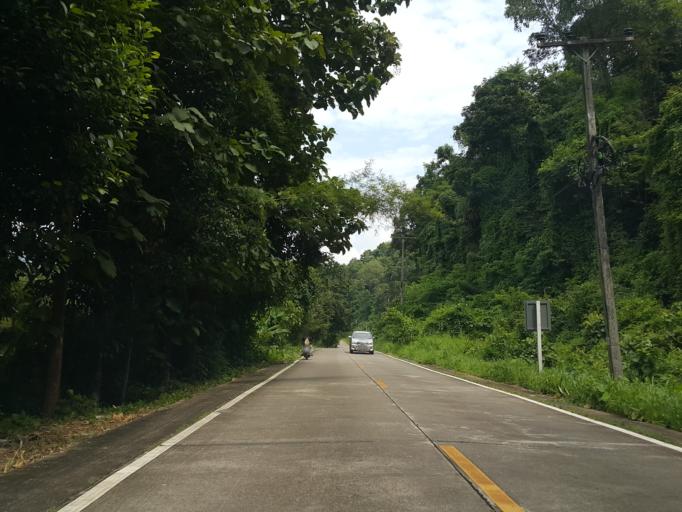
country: TH
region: Mae Hong Son
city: Mae Hong Son
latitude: 19.4537
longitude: 97.9660
